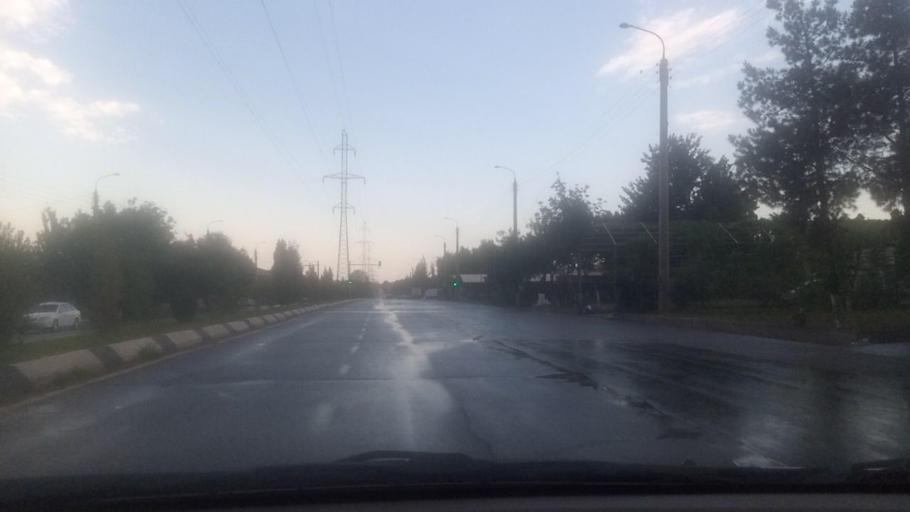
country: UZ
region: Toshkent Shahri
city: Tashkent
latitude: 41.3135
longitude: 69.1933
